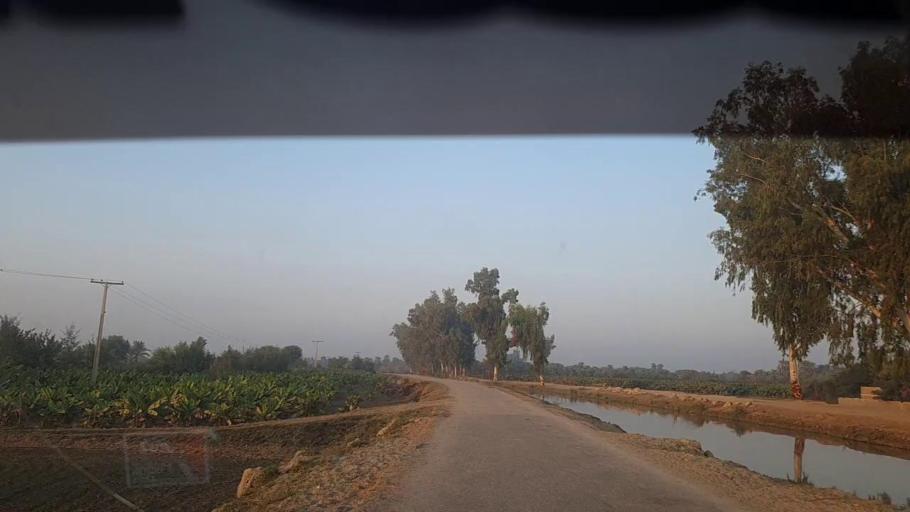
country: PK
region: Sindh
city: Ranipur
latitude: 27.2346
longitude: 68.5488
